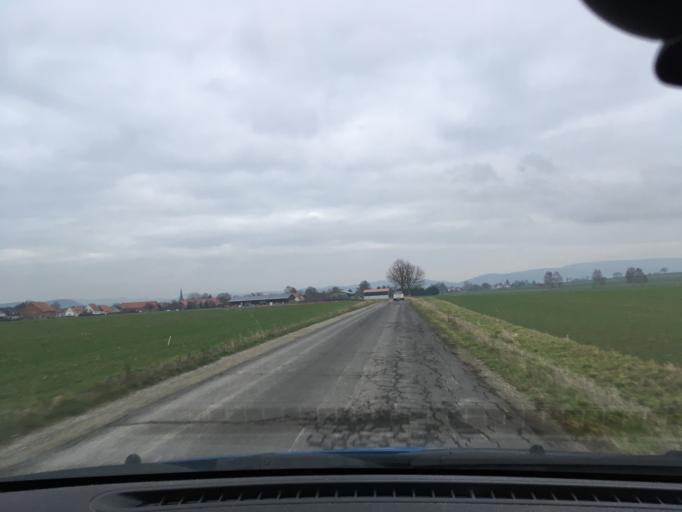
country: DE
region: Lower Saxony
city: Hardegsen
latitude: 51.6375
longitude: 9.8594
